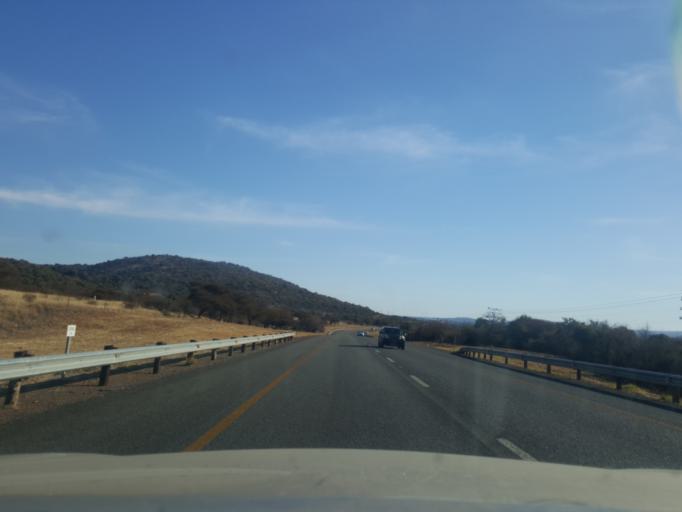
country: ZA
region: North-West
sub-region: Ngaka Modiri Molema District Municipality
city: Zeerust
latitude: -25.5389
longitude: 26.1240
